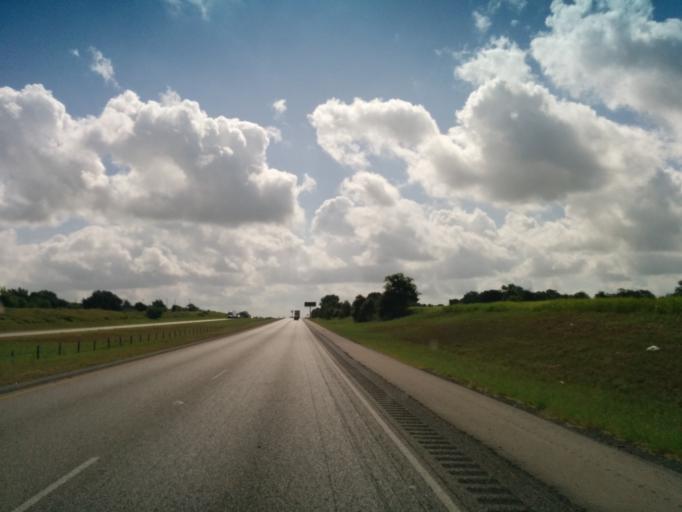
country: US
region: Texas
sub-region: Fayette County
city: Schulenburg
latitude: 29.6897
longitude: -96.9368
